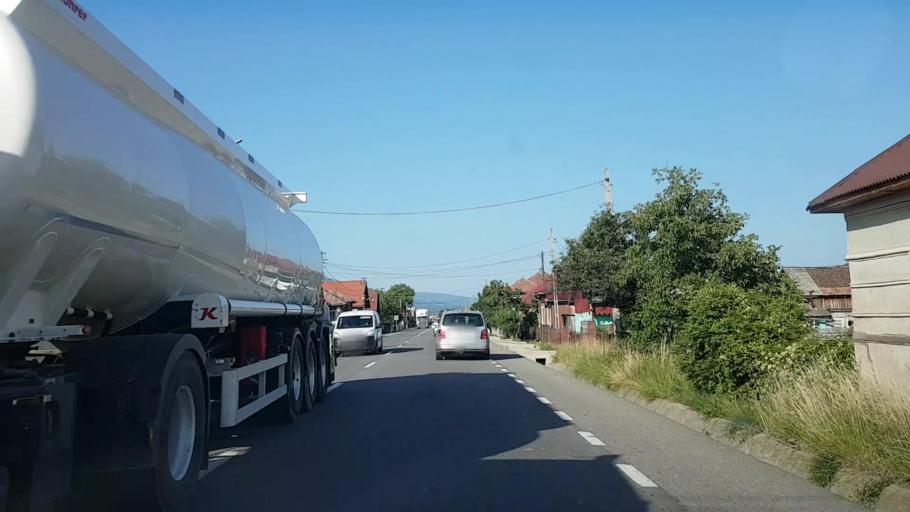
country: RO
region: Bistrita-Nasaud
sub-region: Comuna Josenii Bargaului
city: Josenii Bargaului
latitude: 47.1978
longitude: 24.6333
